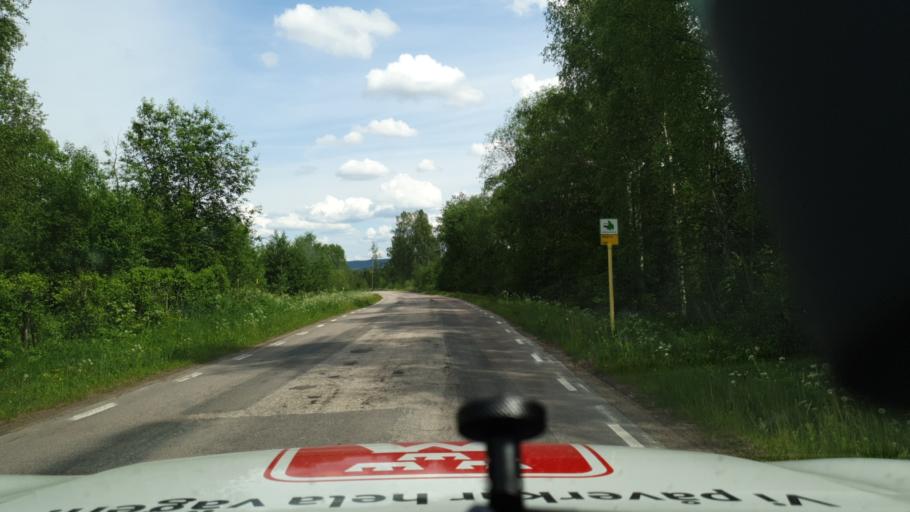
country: SE
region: Vaermland
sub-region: Torsby Kommun
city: Torsby
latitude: 59.9839
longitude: 12.8313
